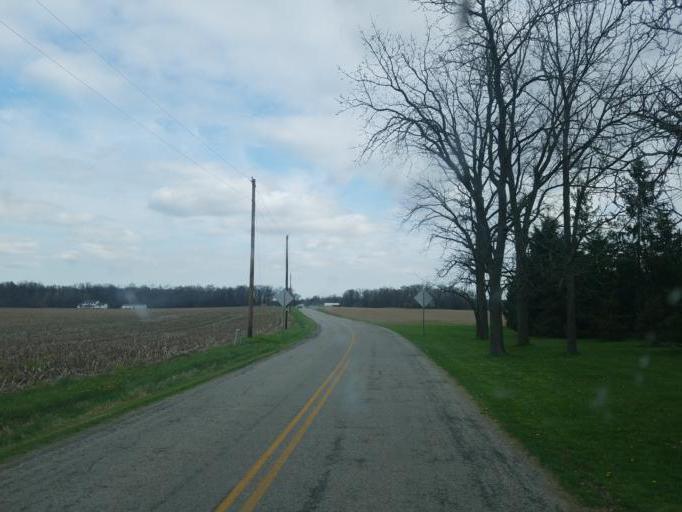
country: US
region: Ohio
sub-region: Morrow County
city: Cardington
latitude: 40.6028
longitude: -82.9778
